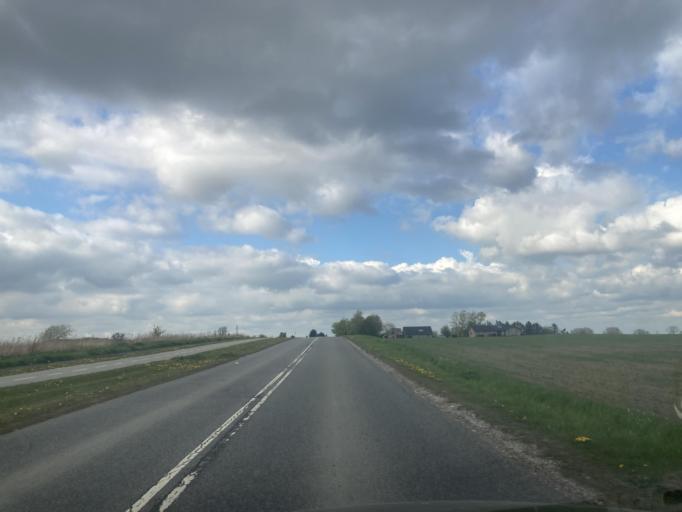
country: DK
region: Zealand
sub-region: Greve Kommune
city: Tune
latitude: 55.6031
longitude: 12.1791
